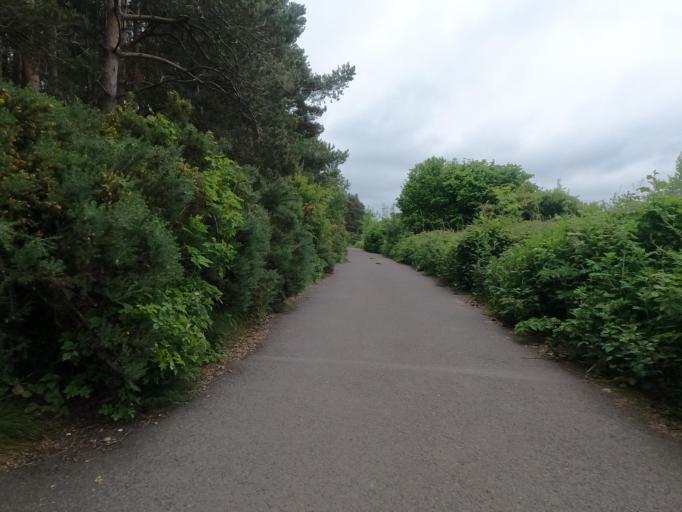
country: GB
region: England
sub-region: Northumberland
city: Bedlington
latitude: 55.1238
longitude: -1.5651
